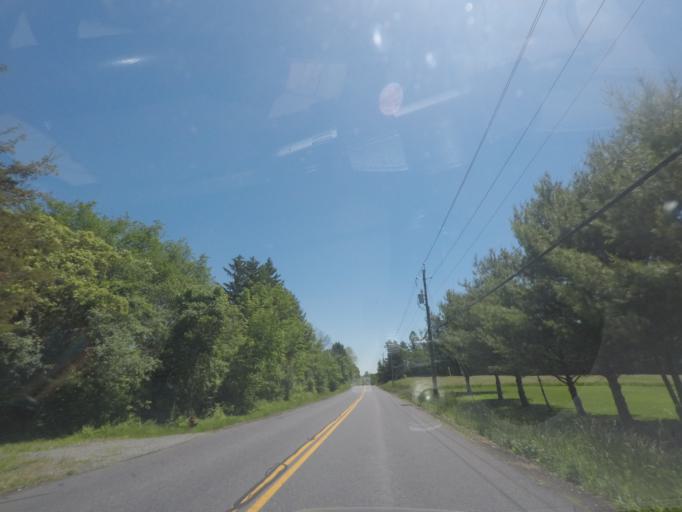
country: US
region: New York
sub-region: Saratoga County
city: Stillwater
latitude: 42.9364
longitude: -73.6858
